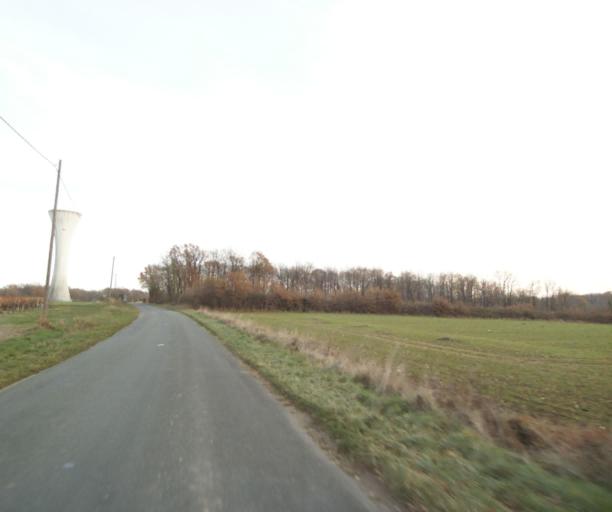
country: FR
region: Poitou-Charentes
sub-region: Departement de la Charente-Maritime
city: Fontcouverte
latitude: 45.7998
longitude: -0.5753
